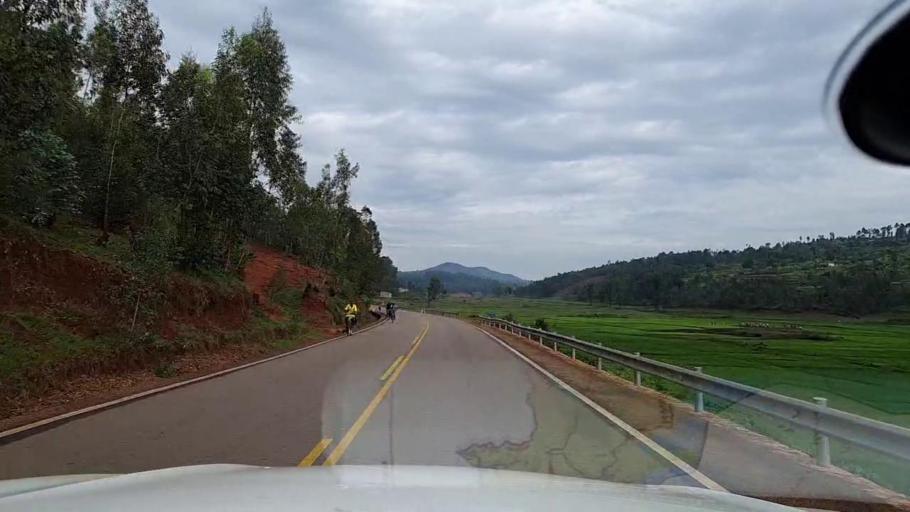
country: RW
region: Southern Province
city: Butare
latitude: -2.5677
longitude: 29.7282
